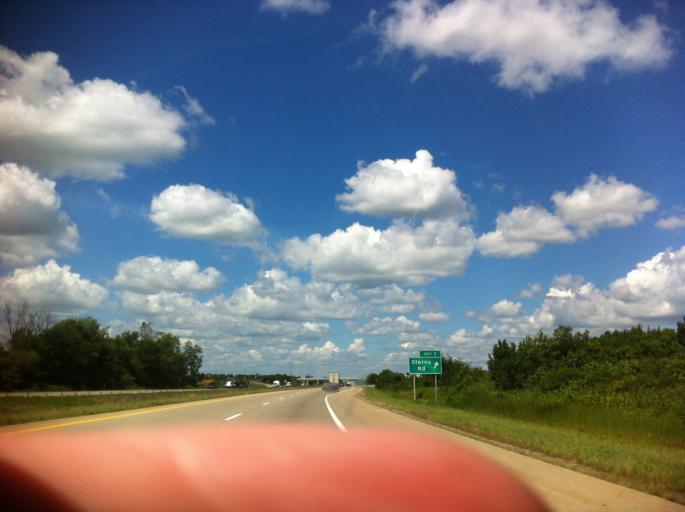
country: US
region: Ohio
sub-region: Lucas County
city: Sylvania
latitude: 41.7415
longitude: -83.6937
